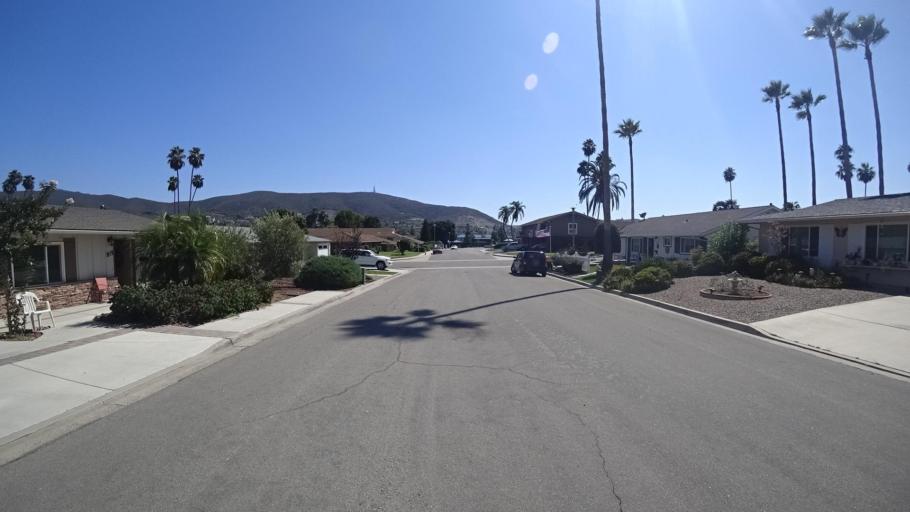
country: US
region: California
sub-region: San Diego County
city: Lake San Marcos
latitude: 33.1266
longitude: -117.2063
